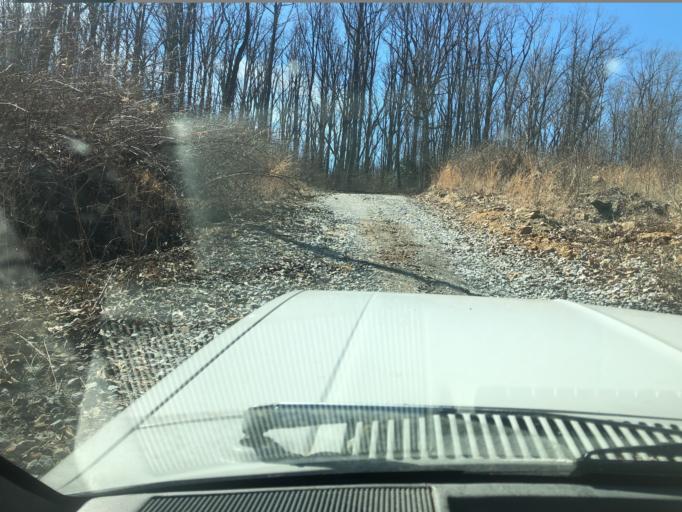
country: US
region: Tennessee
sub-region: Roane County
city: Rockwood
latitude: 35.9791
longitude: -84.7466
